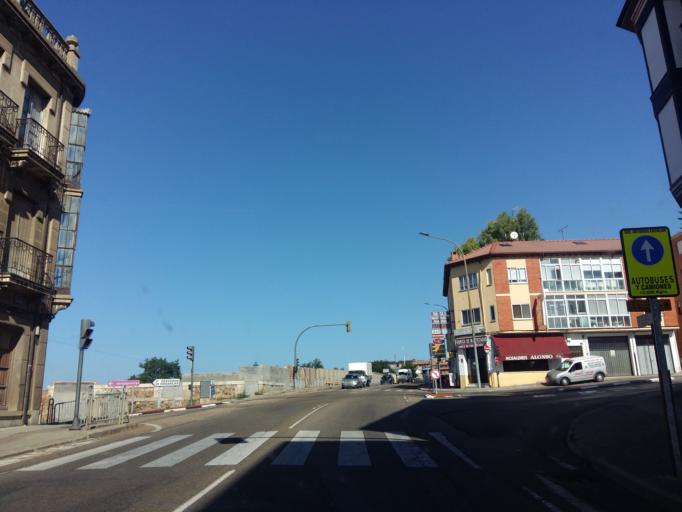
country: ES
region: Castille and Leon
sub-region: Provincia de Leon
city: Astorga
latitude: 42.4556
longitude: -6.0605
